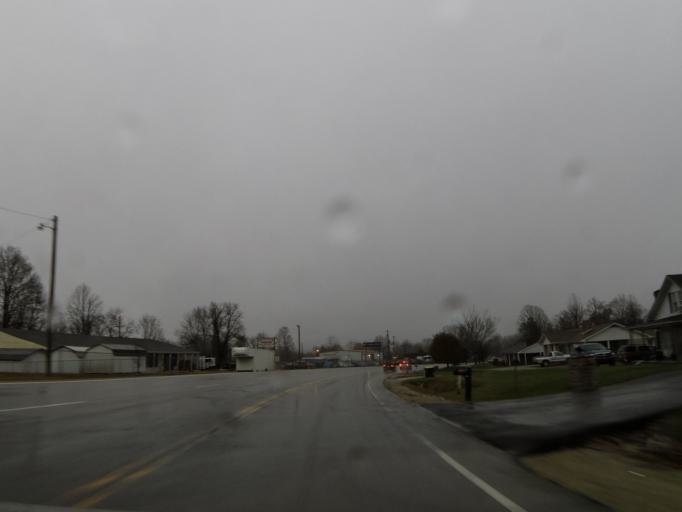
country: US
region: Kentucky
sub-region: Rockcastle County
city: Mount Vernon
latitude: 37.3479
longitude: -84.3187
